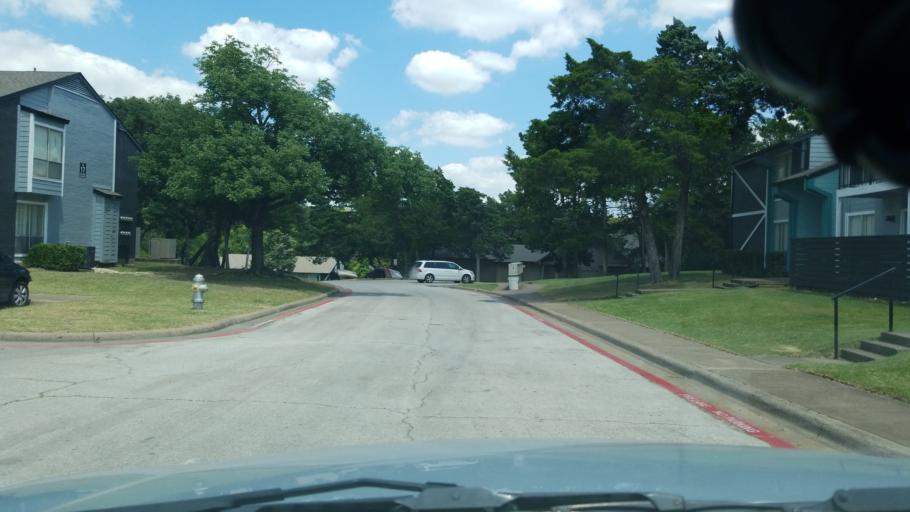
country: US
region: Texas
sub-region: Dallas County
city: Cockrell Hill
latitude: 32.6886
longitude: -96.8623
